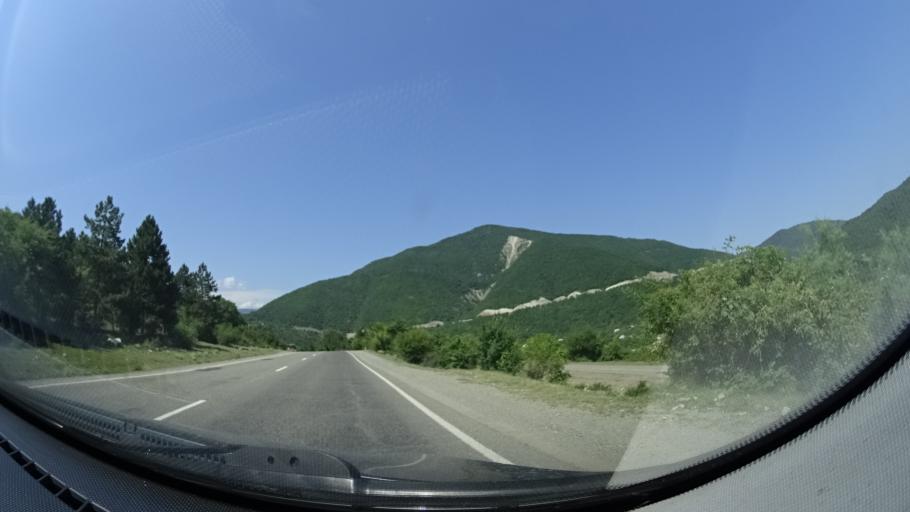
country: GE
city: Zhinvali
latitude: 42.1200
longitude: 44.7758
